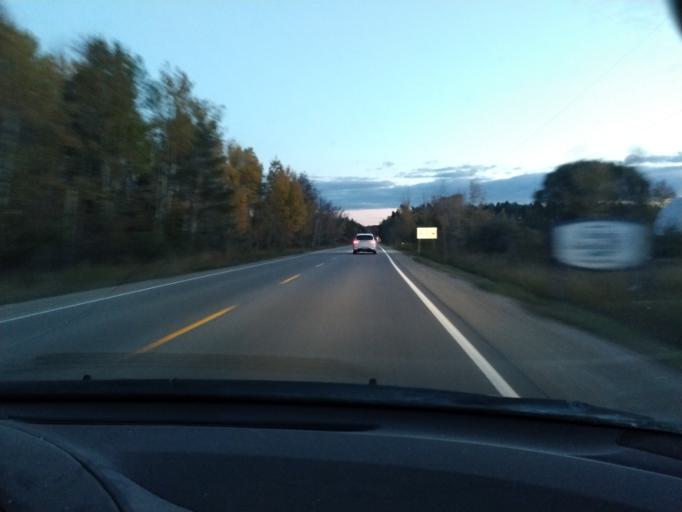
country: CA
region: Ontario
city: Bradford West Gwillimbury
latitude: 44.1771
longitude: -79.6589
